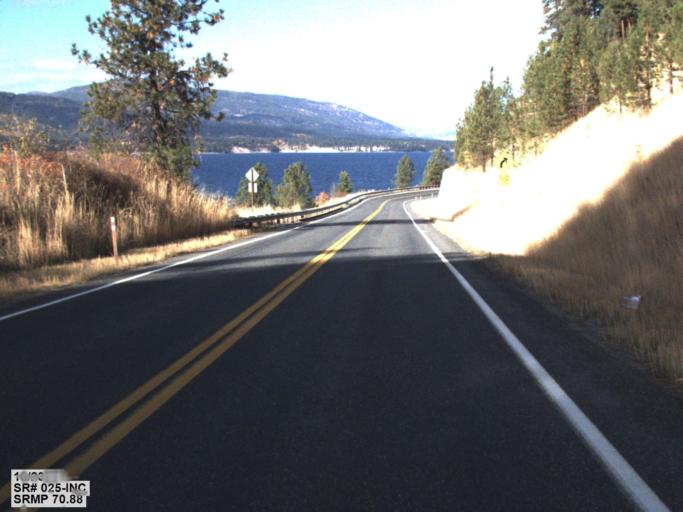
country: US
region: Washington
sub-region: Stevens County
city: Kettle Falls
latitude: 48.4871
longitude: -118.1674
